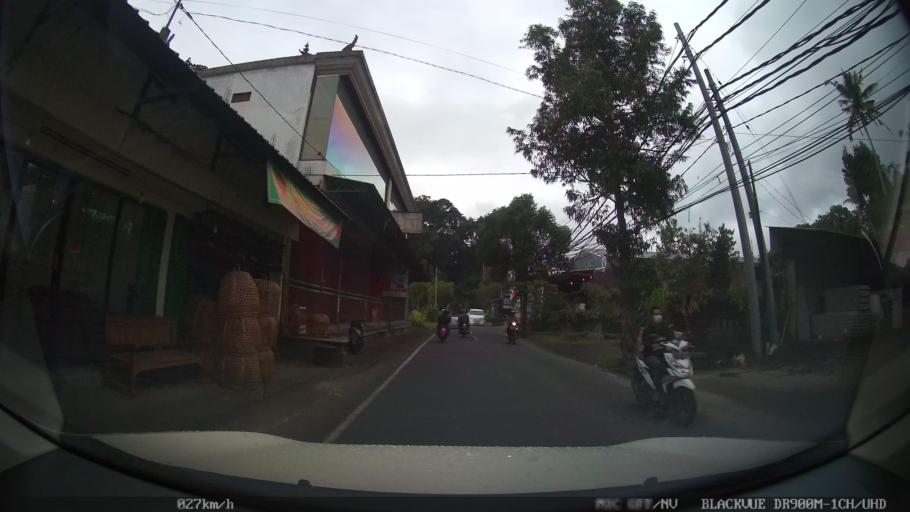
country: ID
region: Bali
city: Bayad
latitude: -8.4449
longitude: 115.2421
